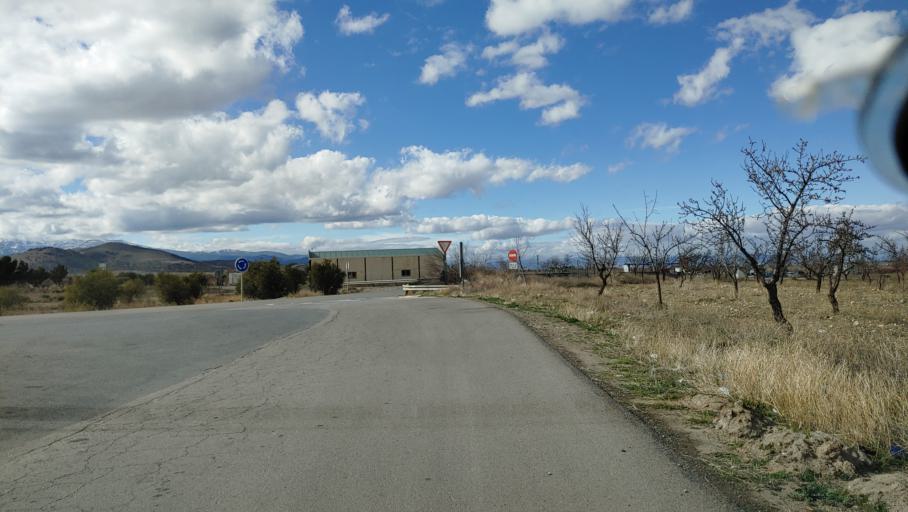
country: ES
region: Andalusia
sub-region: Provincia de Granada
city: Hueneja
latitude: 37.1960
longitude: -2.9850
